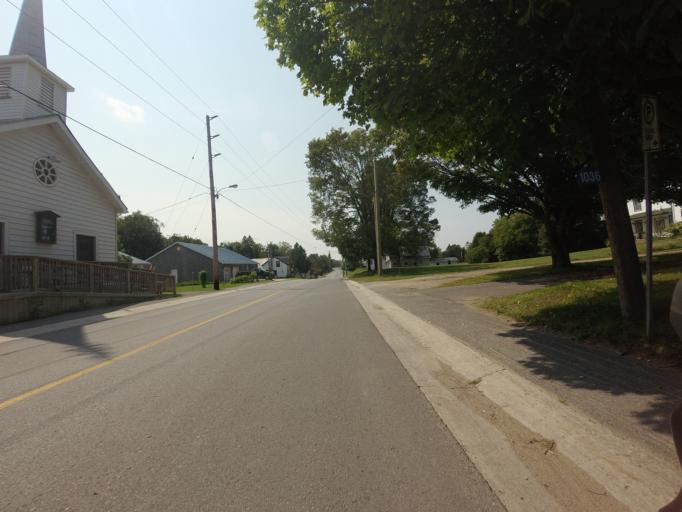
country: CA
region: Ontario
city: Skatepark
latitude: 44.6559
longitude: -76.7189
